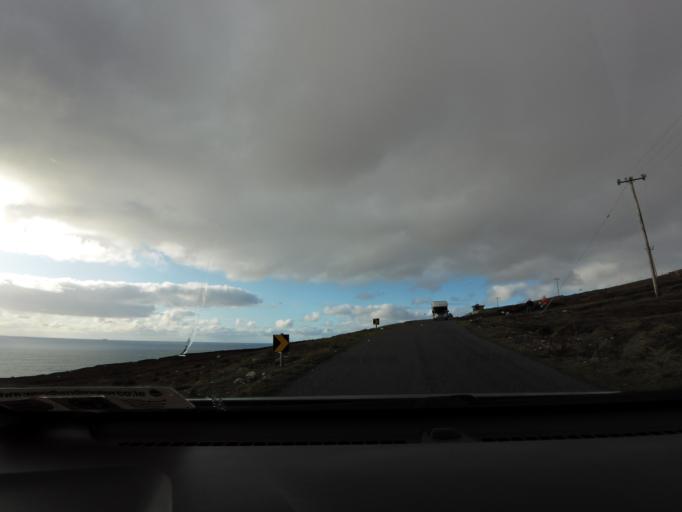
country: IE
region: Connaught
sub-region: Maigh Eo
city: Belmullet
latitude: 53.9067
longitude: -9.9951
